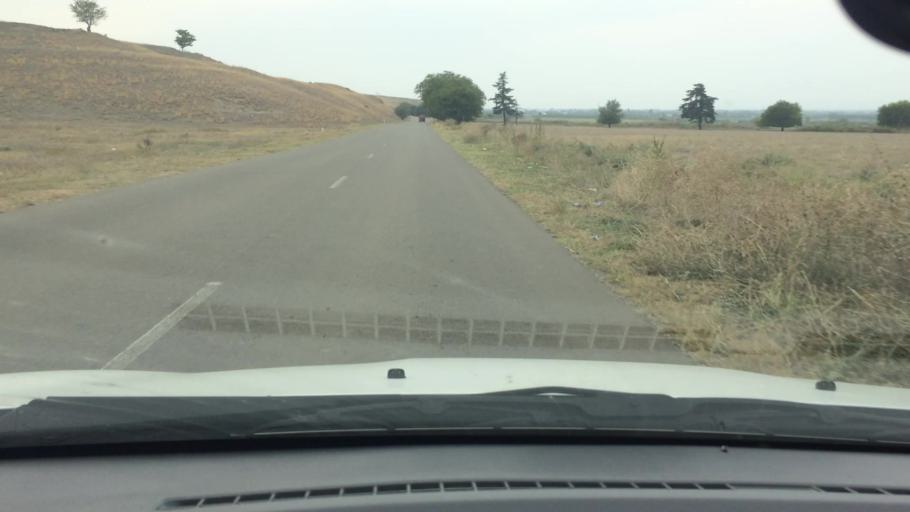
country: AM
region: Tavush
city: Berdavan
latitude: 41.3379
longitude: 45.0074
